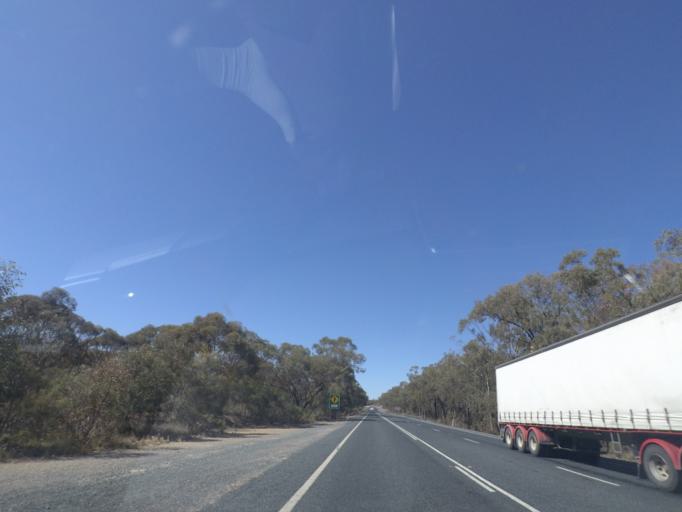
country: AU
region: New South Wales
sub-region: Bland
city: West Wyalong
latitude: -34.1333
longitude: 147.1227
